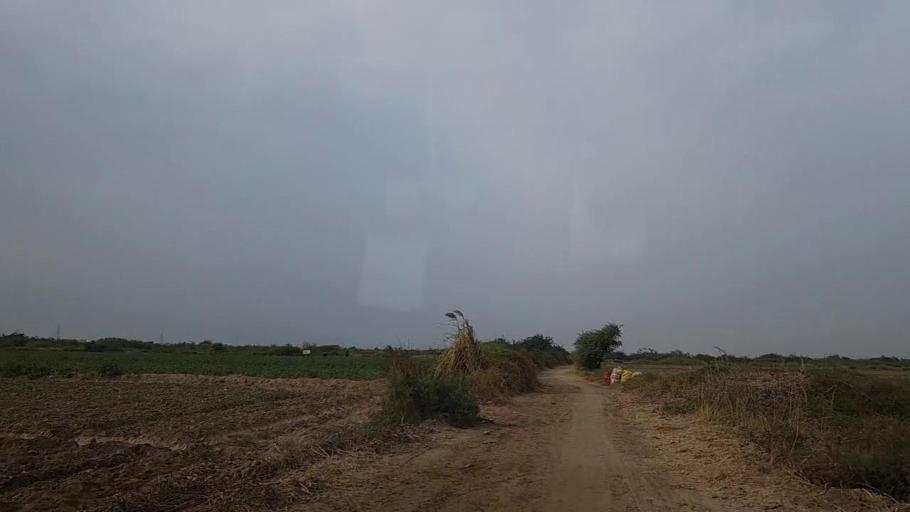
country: PK
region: Sindh
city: Mirpur Sakro
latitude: 24.6188
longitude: 67.5039
